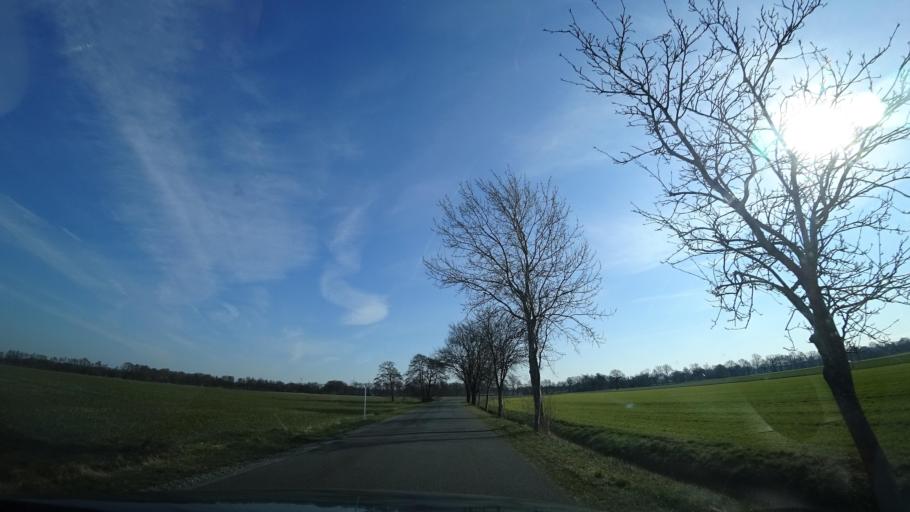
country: DE
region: Lower Saxony
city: Hatten
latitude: 53.0593
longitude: 8.3303
